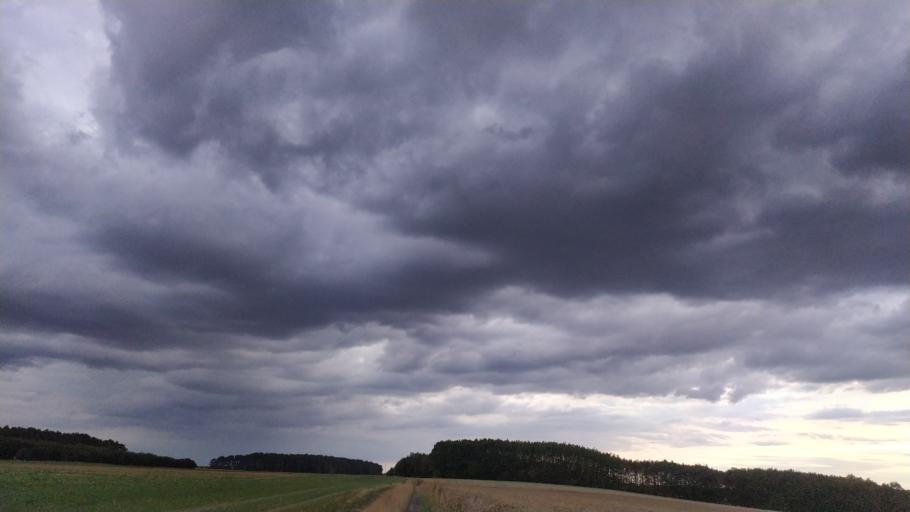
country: DE
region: Mecklenburg-Vorpommern
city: Wolgast
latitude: 54.0494
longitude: 13.8120
